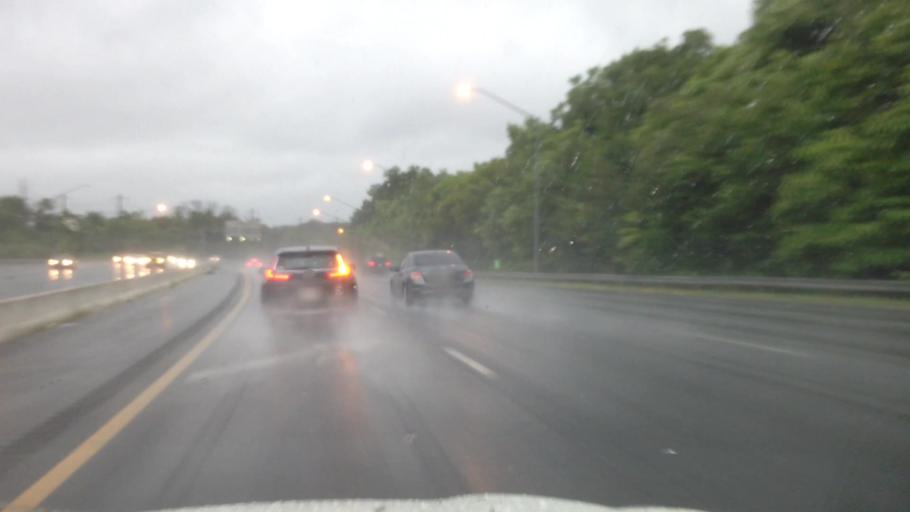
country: US
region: Maryland
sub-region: Prince George's County
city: Landover Hills
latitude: 38.9413
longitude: -76.8836
